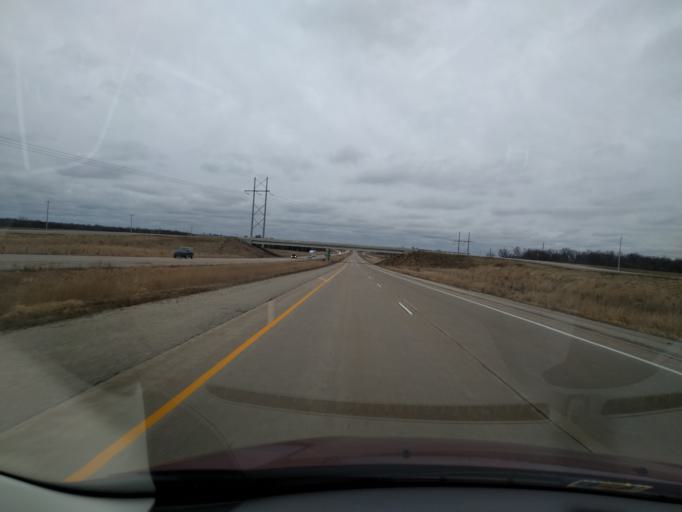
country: US
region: Wisconsin
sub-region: Winnebago County
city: Winneconne
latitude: 44.1717
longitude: -88.6645
